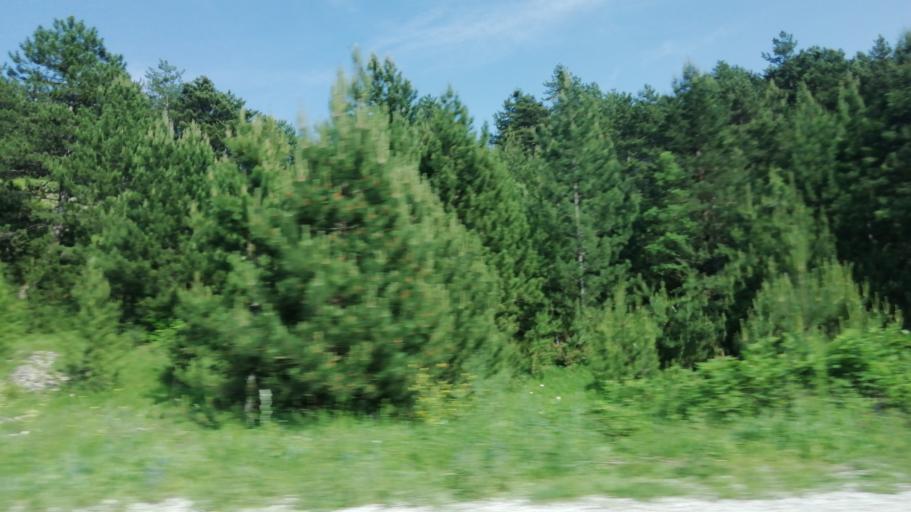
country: TR
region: Karabuk
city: Karabuk
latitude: 41.1221
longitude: 32.5849
